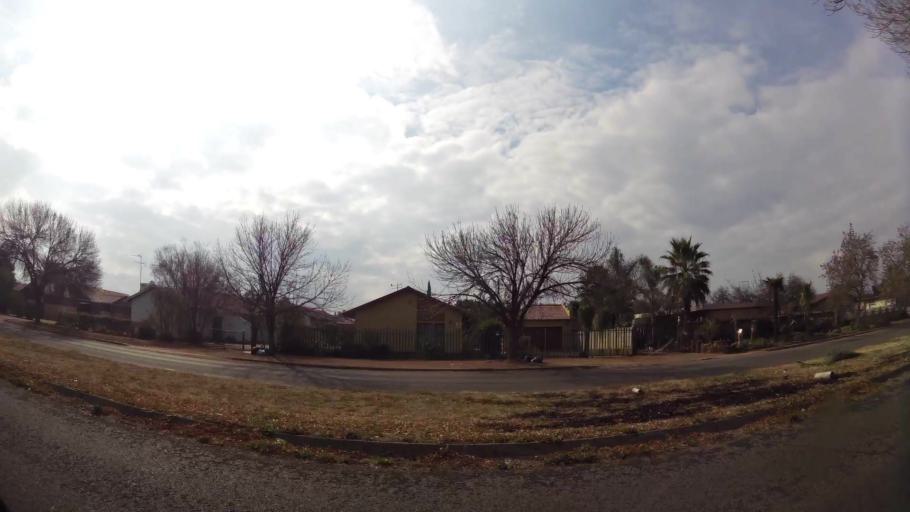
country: ZA
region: Gauteng
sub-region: Sedibeng District Municipality
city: Vanderbijlpark
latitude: -26.6904
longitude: 27.8465
